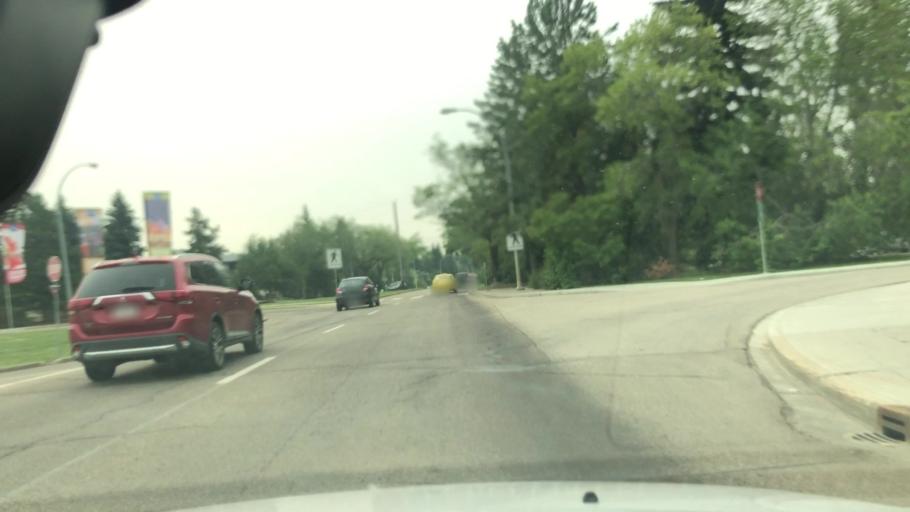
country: CA
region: Alberta
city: Edmonton
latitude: 53.5229
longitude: -113.5411
